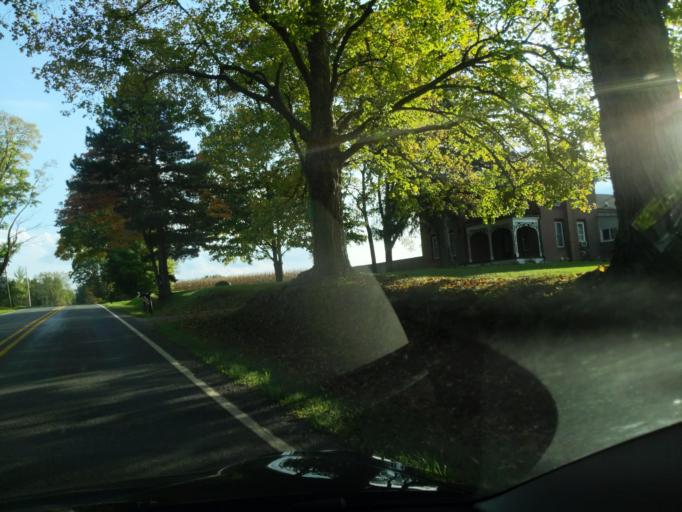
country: US
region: Michigan
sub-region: Ingham County
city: Leslie
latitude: 42.3678
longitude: -84.4629
